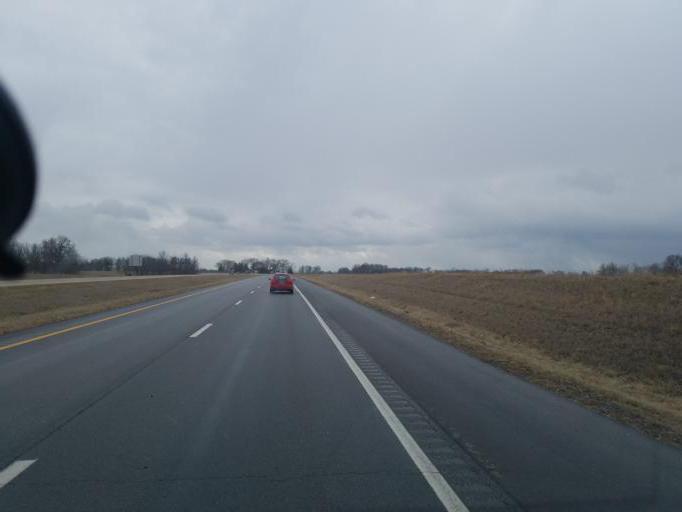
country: US
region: Missouri
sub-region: Randolph County
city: Moberly
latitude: 39.3821
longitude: -92.4138
